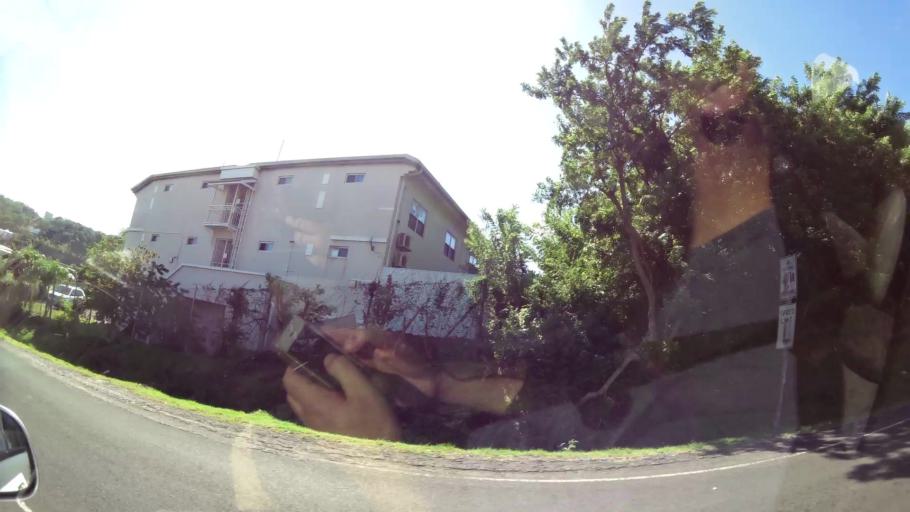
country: GD
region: Saint George
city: Saint George's
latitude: 12.0098
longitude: -61.7659
